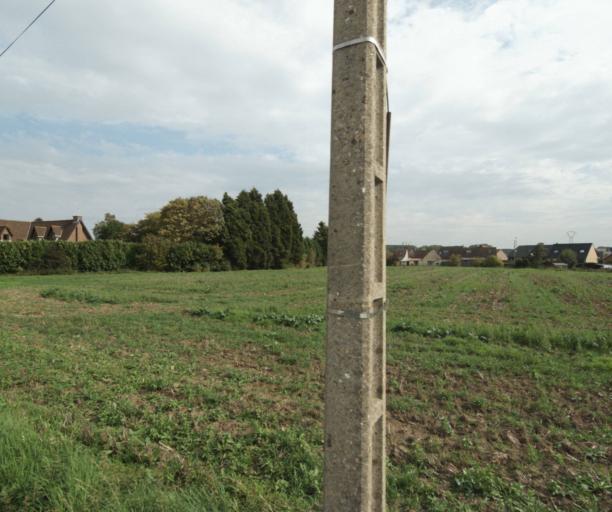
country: FR
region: Nord-Pas-de-Calais
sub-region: Departement du Nord
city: Marquillies
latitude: 50.5400
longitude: 2.8728
